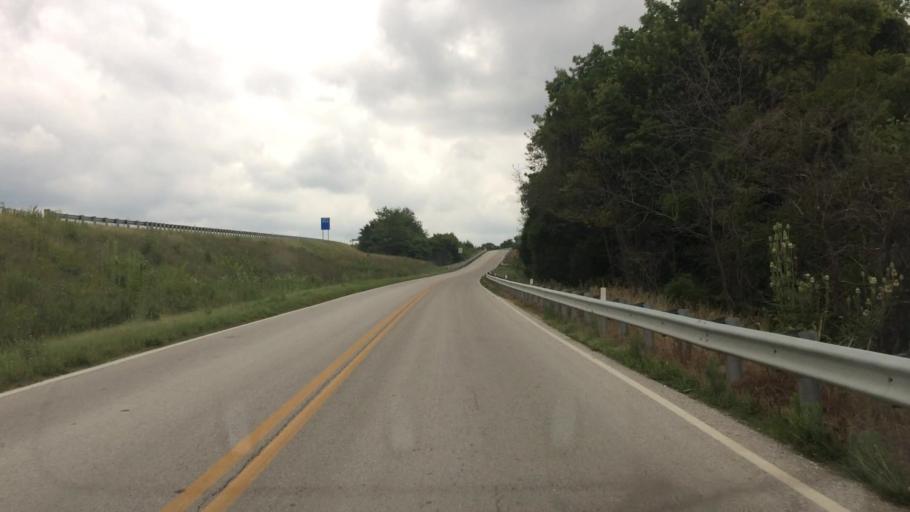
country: US
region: Missouri
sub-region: Webster County
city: Marshfield
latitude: 37.3033
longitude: -92.9954
